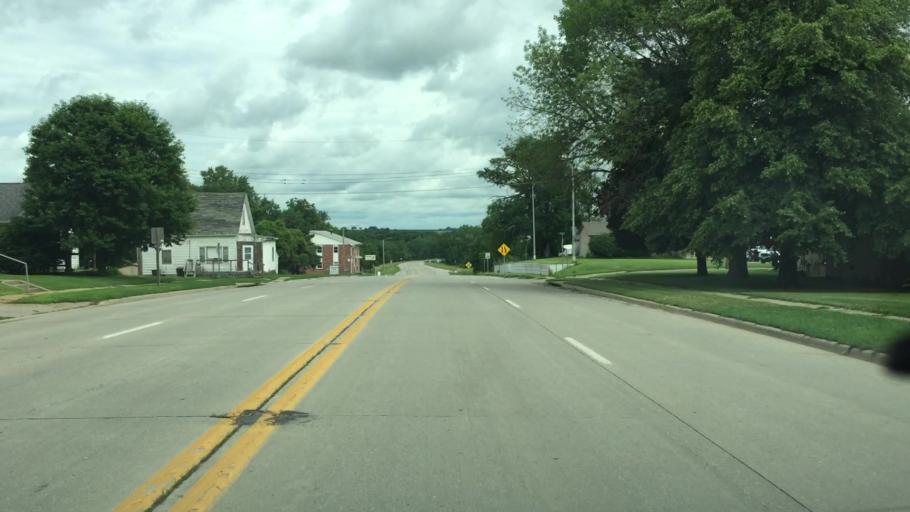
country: US
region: Iowa
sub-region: Jasper County
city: Monroe
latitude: 41.5262
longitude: -93.1018
